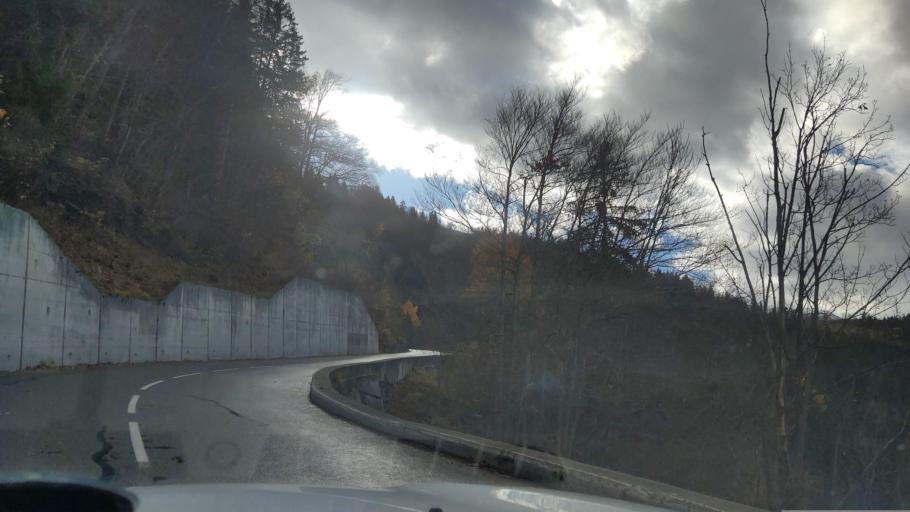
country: FR
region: Rhone-Alpes
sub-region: Departement de la Savoie
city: Villargondran
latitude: 45.2279
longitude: 6.3349
